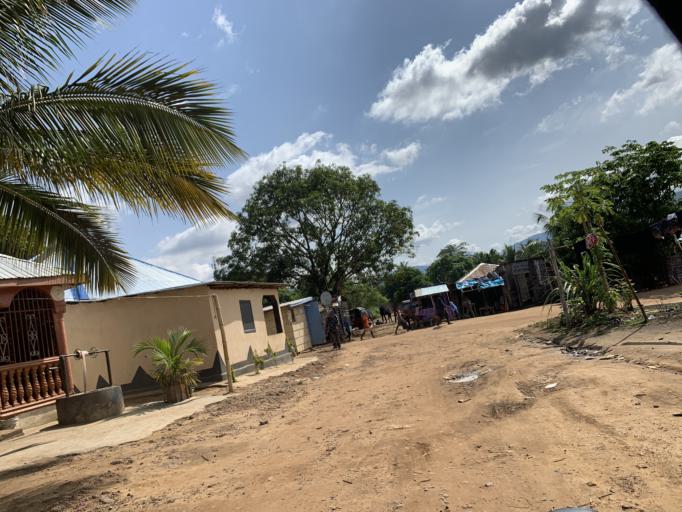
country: SL
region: Western Area
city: Waterloo
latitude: 8.3310
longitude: -13.0525
